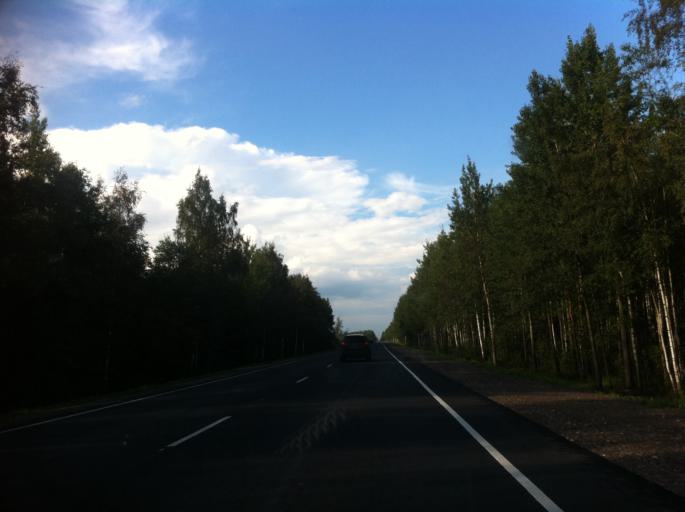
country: RU
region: Leningrad
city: Luga
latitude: 58.4457
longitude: 29.7549
